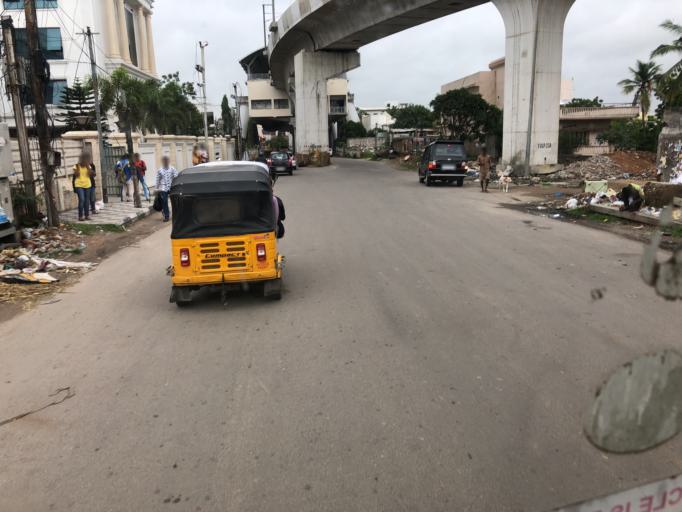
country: IN
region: Telangana
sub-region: Hyderabad
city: Hyderabad
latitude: 17.4295
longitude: 78.4248
